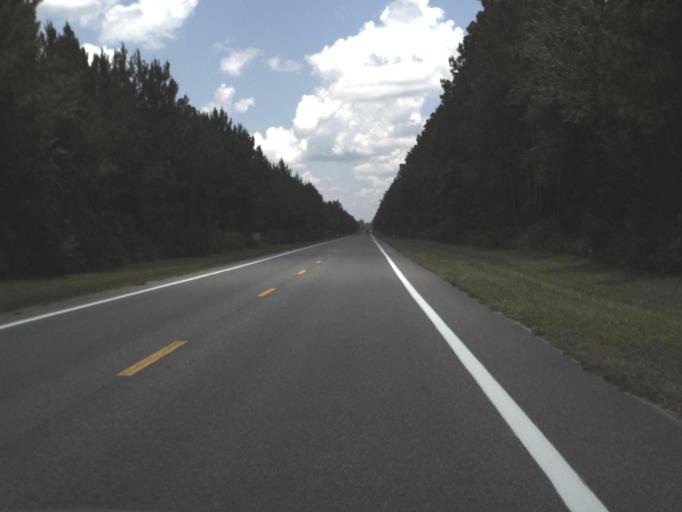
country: US
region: Florida
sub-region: Union County
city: Lake Butler
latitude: 30.1213
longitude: -82.2078
